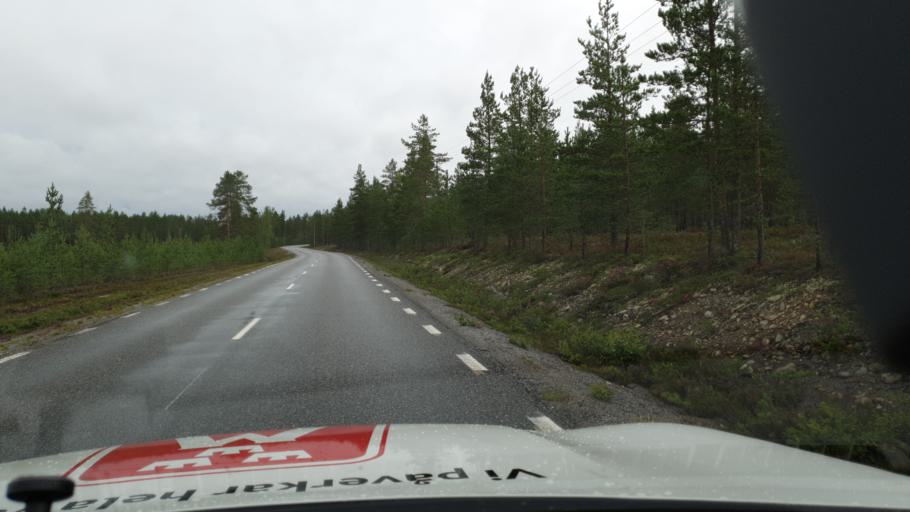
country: SE
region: Vaesterbotten
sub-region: Umea Kommun
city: Saevar
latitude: 63.9637
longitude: 20.5086
